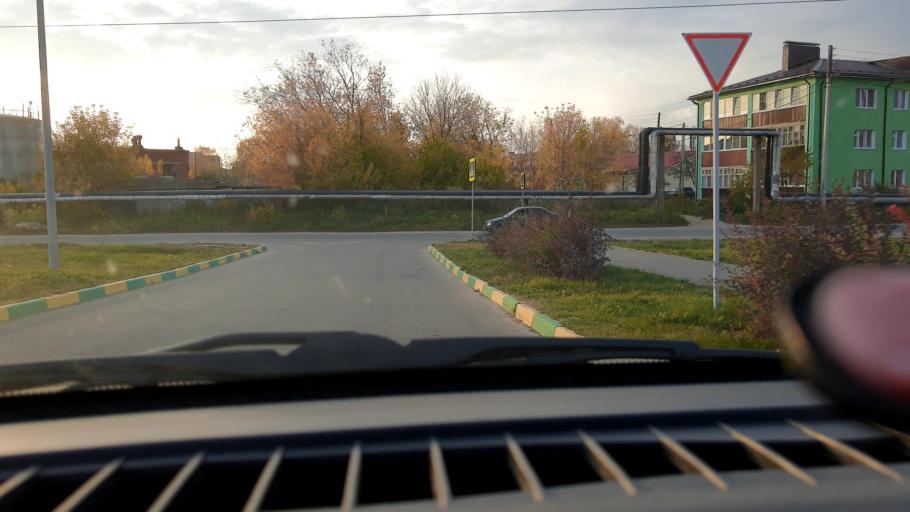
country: RU
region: Nizjnij Novgorod
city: Gorodets
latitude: 56.6394
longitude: 43.4901
